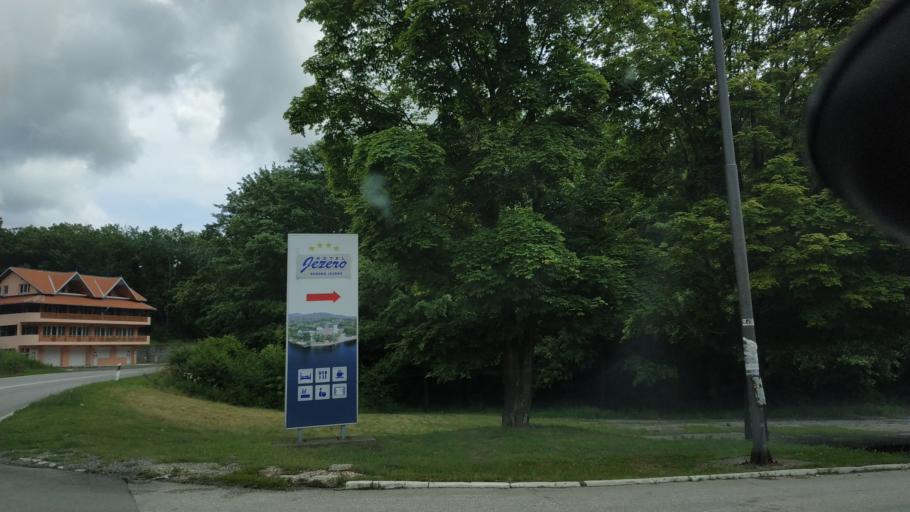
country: RS
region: Central Serbia
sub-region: Borski Okrug
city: Bor
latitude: 44.0919
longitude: 22.0033
